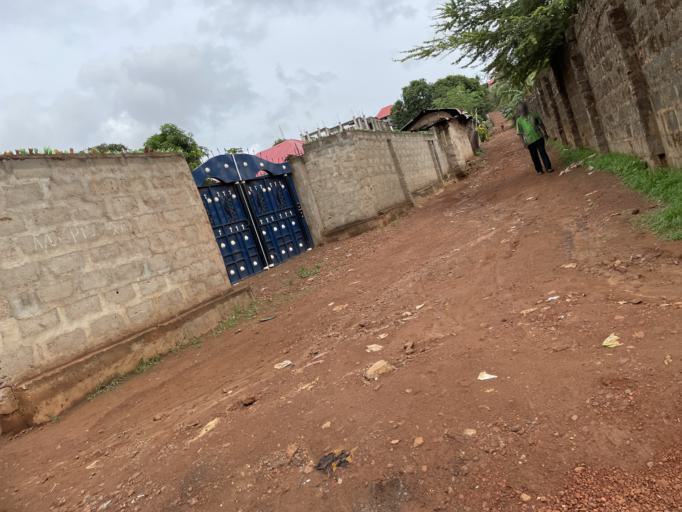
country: SL
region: Western Area
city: Hastings
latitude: 8.4066
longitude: -13.1437
